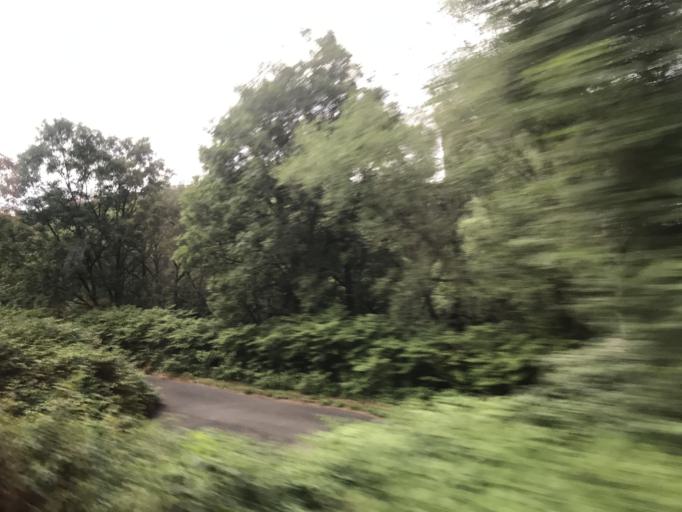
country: DE
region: North Rhine-Westphalia
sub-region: Regierungsbezirk Arnsberg
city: Siegen
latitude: 50.8659
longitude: 8.0044
